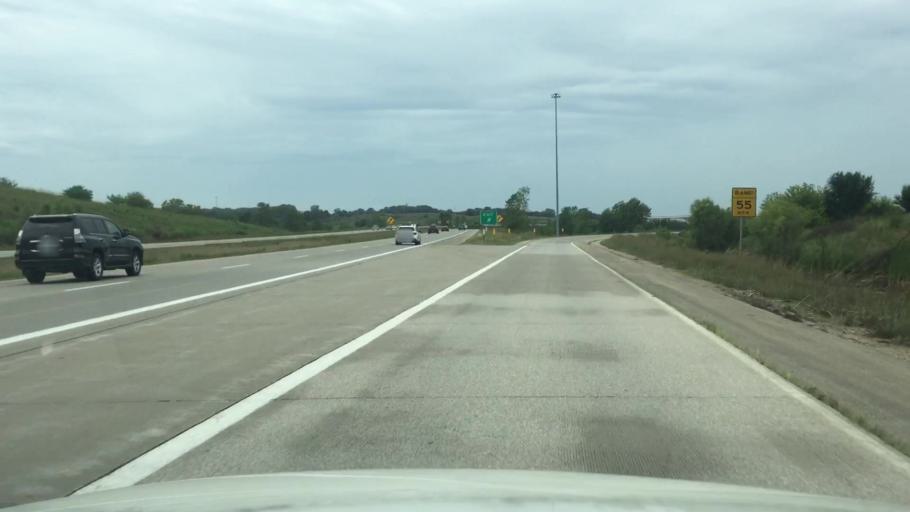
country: US
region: Iowa
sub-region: Polk County
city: West Des Moines
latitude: 41.5230
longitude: -93.7632
